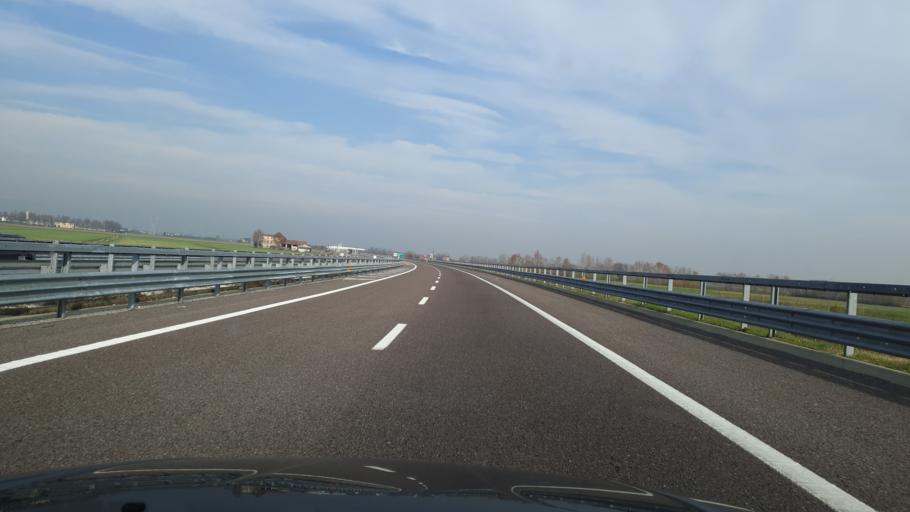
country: IT
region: Veneto
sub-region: Provincia di Padova
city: Bastia
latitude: 45.4029
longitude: 11.6296
